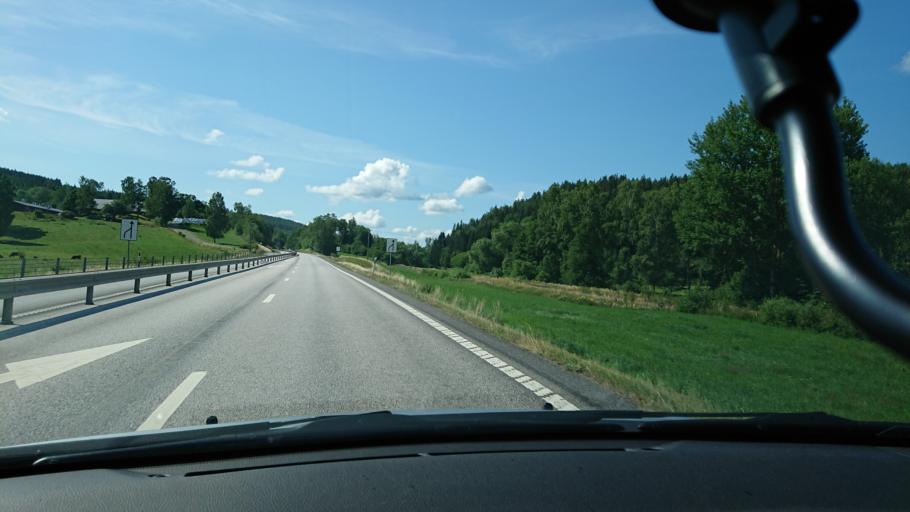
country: SE
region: OEstergoetland
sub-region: Kinda Kommun
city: Kisa
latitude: 58.0428
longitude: 15.6627
